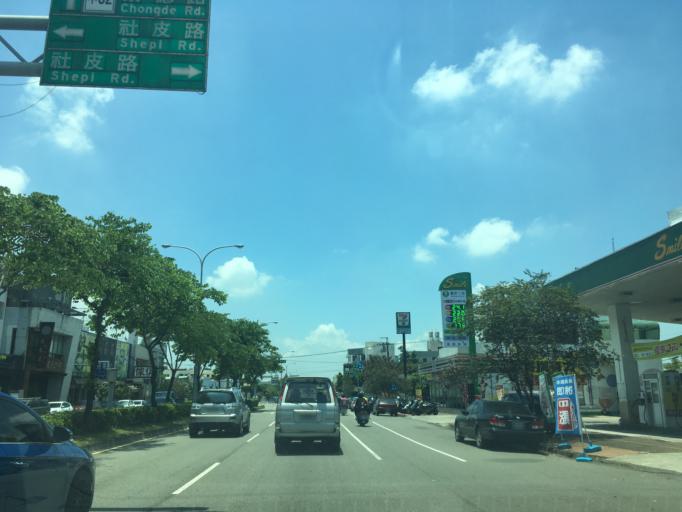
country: TW
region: Taiwan
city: Fengyuan
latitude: 24.2440
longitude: 120.7031
